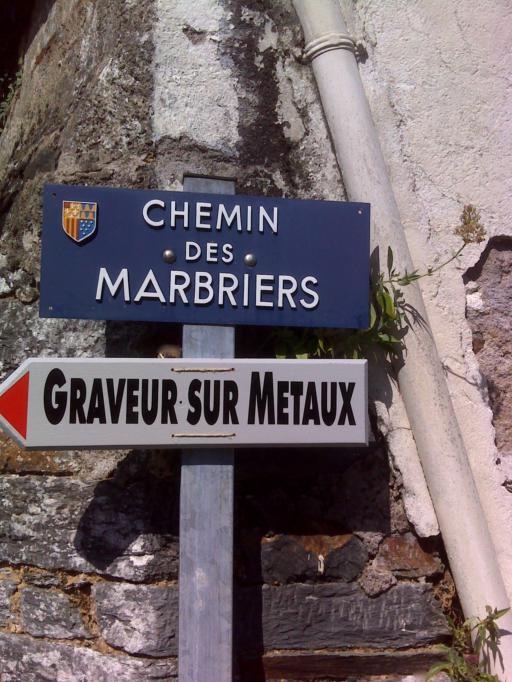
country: FR
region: Brittany
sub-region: Departement du Morbihan
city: La Gacilly
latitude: 47.7615
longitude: -2.1297
